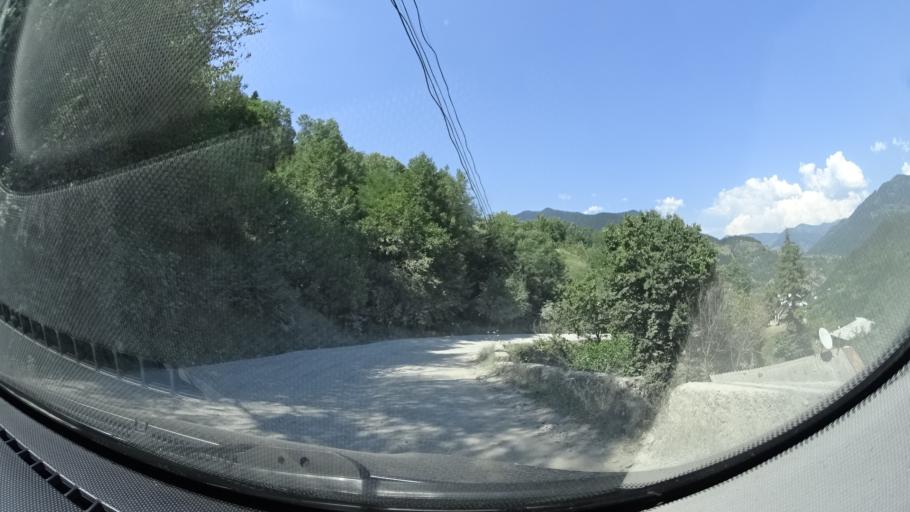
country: GE
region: Ajaria
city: Khulo
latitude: 41.6506
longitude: 42.3227
